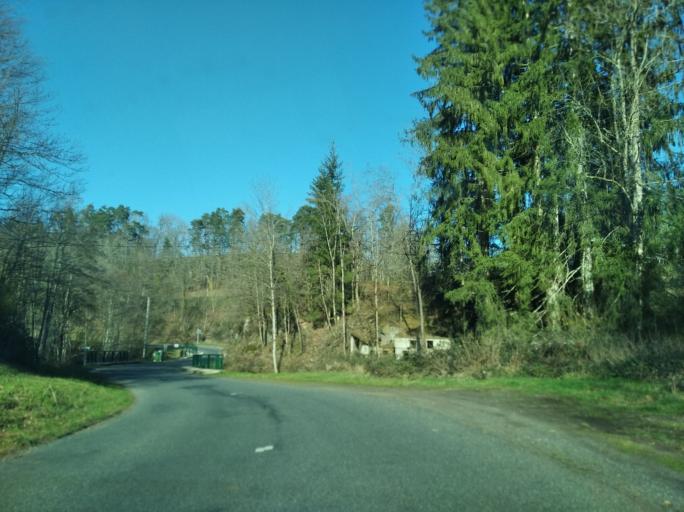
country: FR
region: Auvergne
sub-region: Departement de l'Allier
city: Le Mayet-de-Montagne
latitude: 46.0870
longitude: 3.6813
